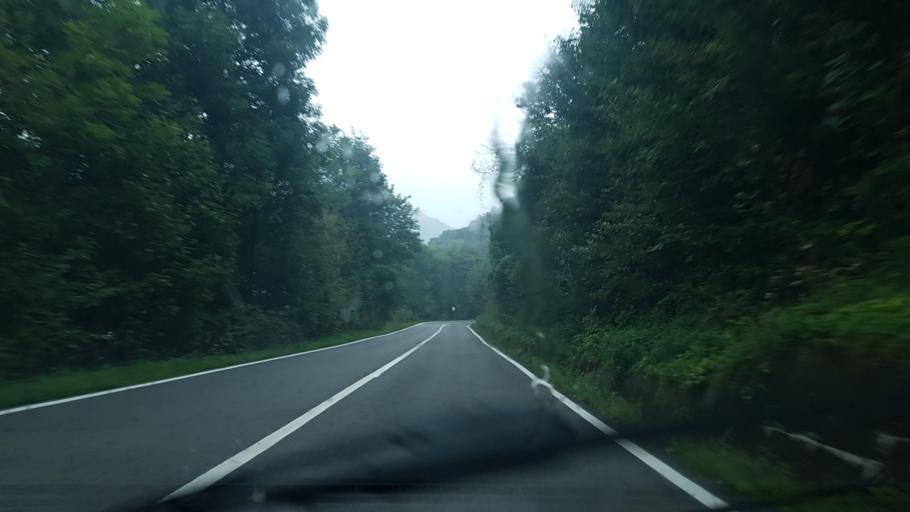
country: IT
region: Piedmont
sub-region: Provincia di Cuneo
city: Frabosa Soprana
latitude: 44.2753
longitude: 7.7671
